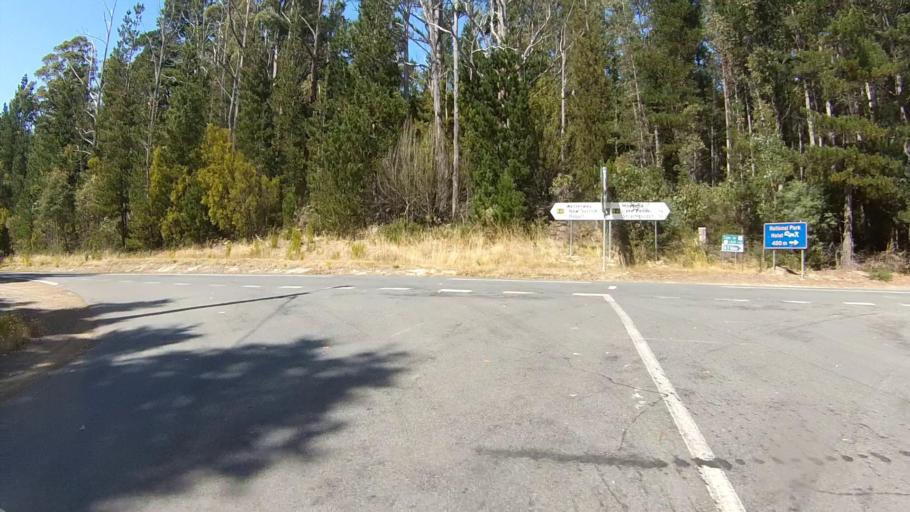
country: AU
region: Tasmania
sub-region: Derwent Valley
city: New Norfolk
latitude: -42.6852
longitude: 146.7225
